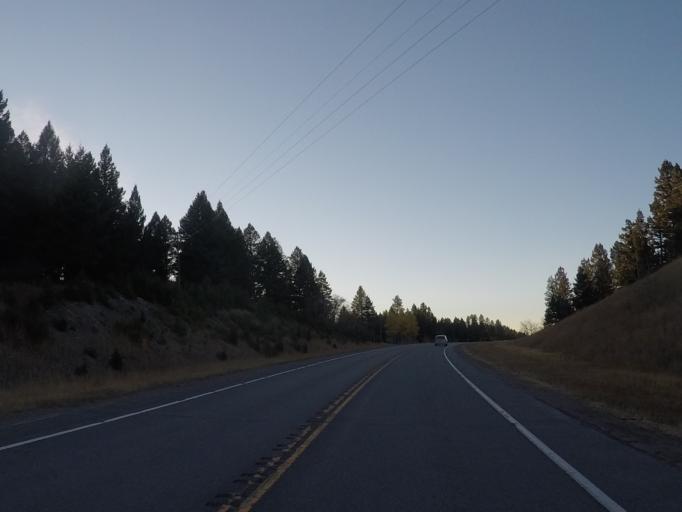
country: US
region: Montana
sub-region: Lewis and Clark County
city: Lincoln
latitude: 47.0088
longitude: -113.0577
